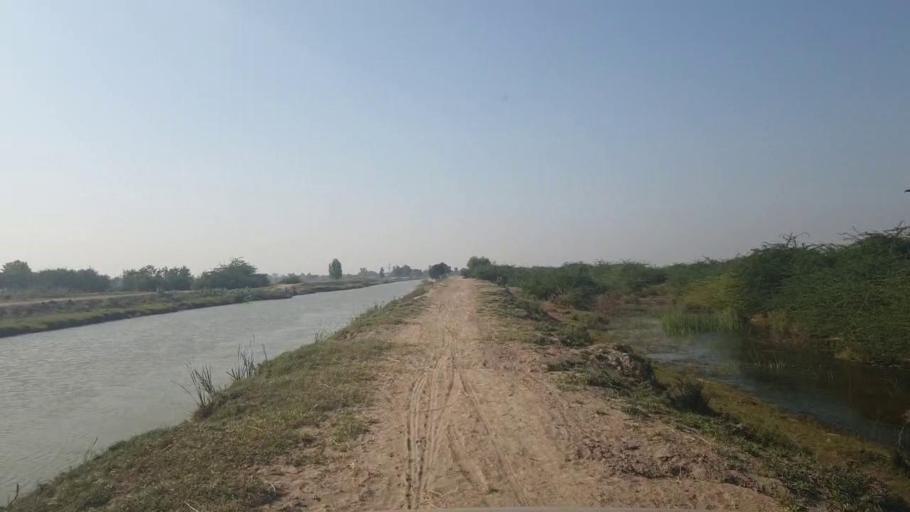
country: PK
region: Sindh
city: Badin
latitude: 24.6931
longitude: 68.8702
